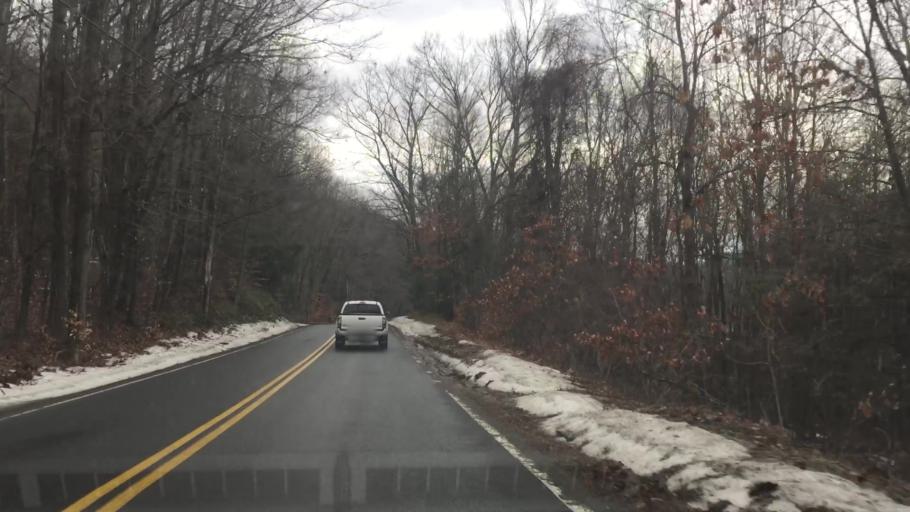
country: US
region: Massachusetts
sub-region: Hampshire County
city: Southampton
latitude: 42.2035
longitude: -72.8461
